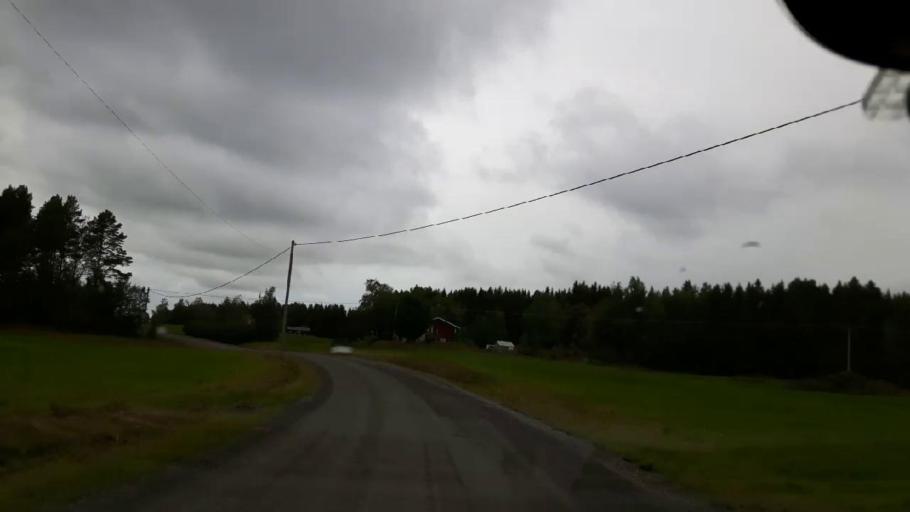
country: SE
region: Jaemtland
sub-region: OEstersunds Kommun
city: Ostersund
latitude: 63.0462
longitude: 14.5745
